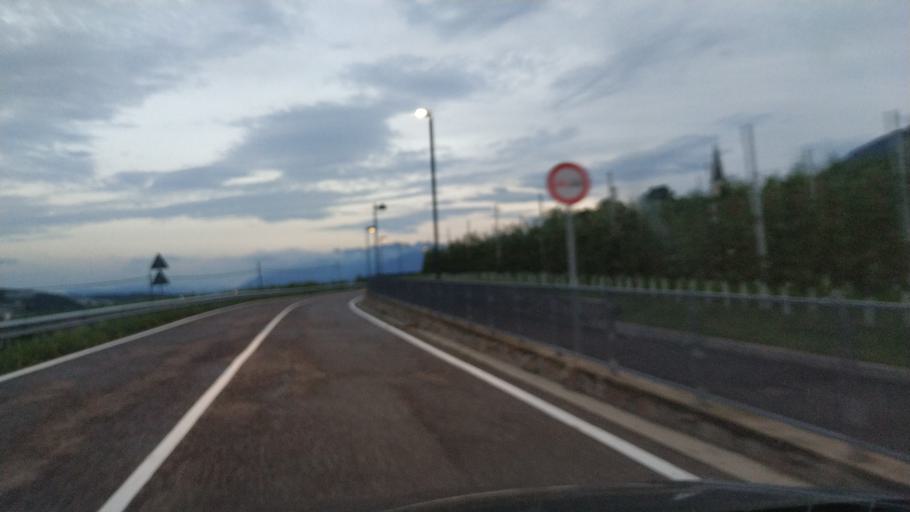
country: IT
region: Trentino-Alto Adige
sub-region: Provincia di Trento
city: Brez
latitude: 46.4295
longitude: 11.1028
